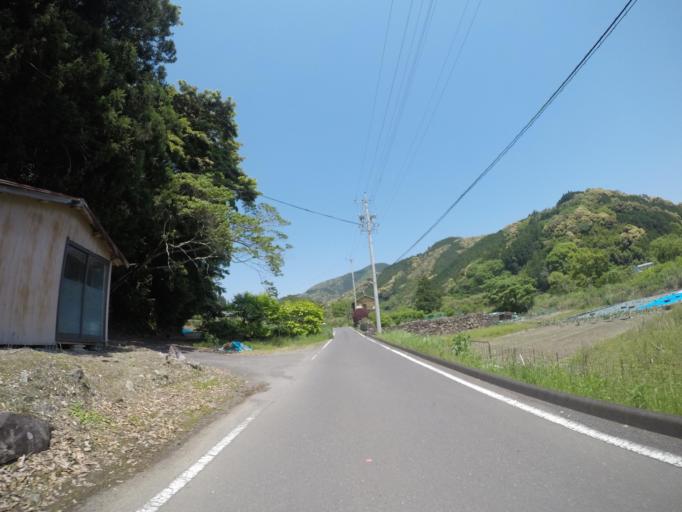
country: JP
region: Shizuoka
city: Shizuoka-shi
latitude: 35.0083
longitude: 138.2734
